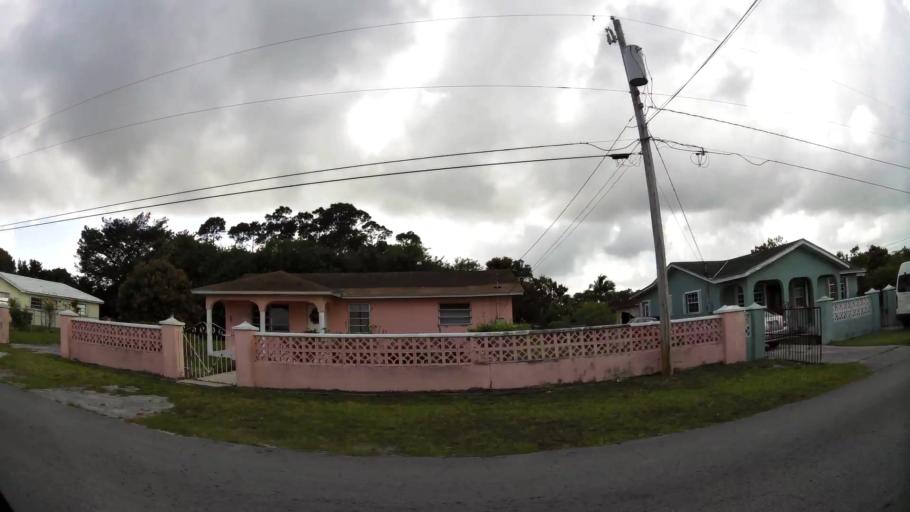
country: BS
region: Freeport
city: Freeport
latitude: 26.5327
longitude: -78.7023
